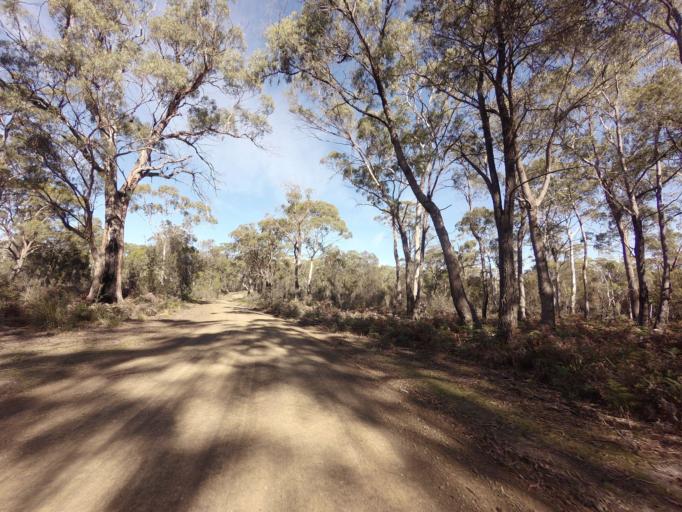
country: AU
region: Tasmania
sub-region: Clarence
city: Sandford
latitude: -42.9588
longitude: 147.7039
